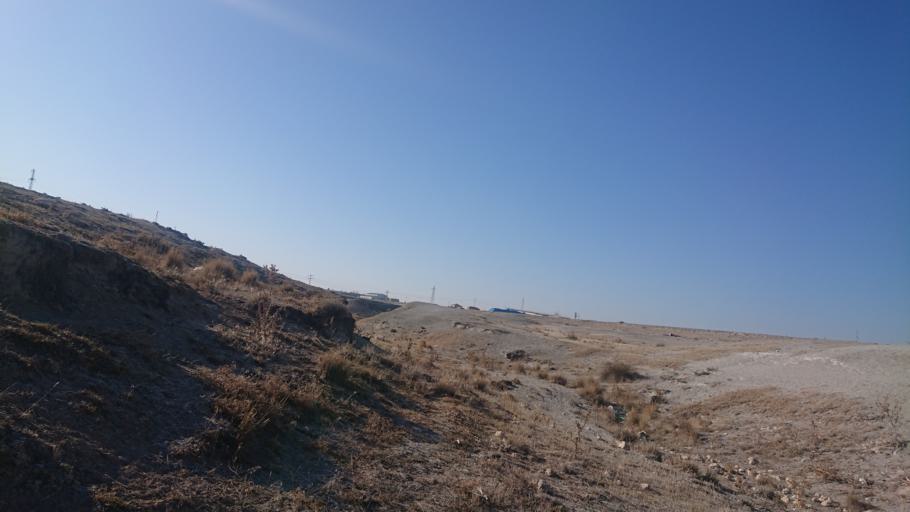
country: TR
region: Aksaray
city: Sultanhani
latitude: 38.2599
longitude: 33.5106
